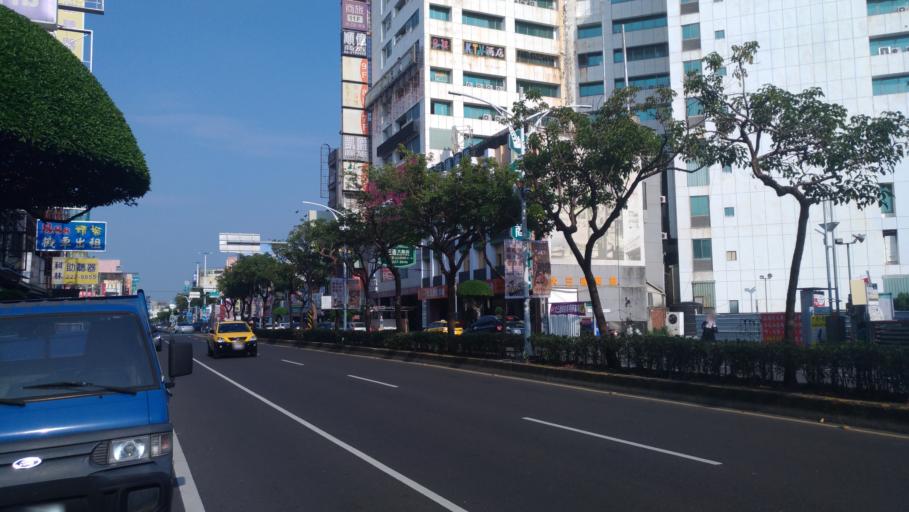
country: TW
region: Taiwan
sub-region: Chiayi
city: Jiayi Shi
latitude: 23.4779
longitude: 120.4407
